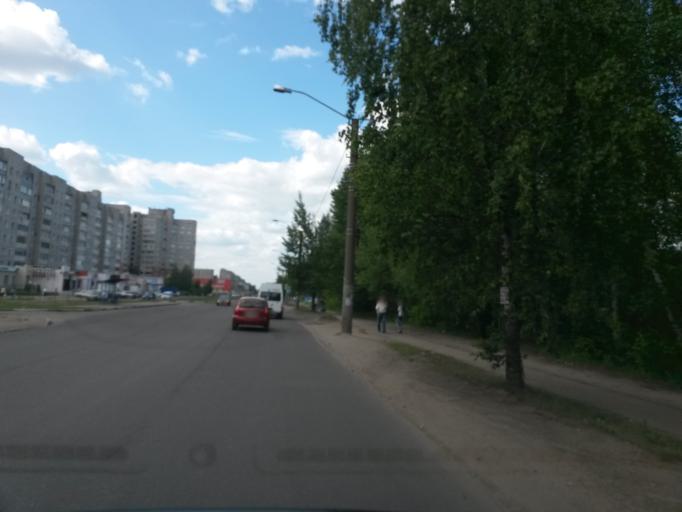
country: RU
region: Jaroslavl
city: Yaroslavl
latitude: 57.6421
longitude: 39.9594
